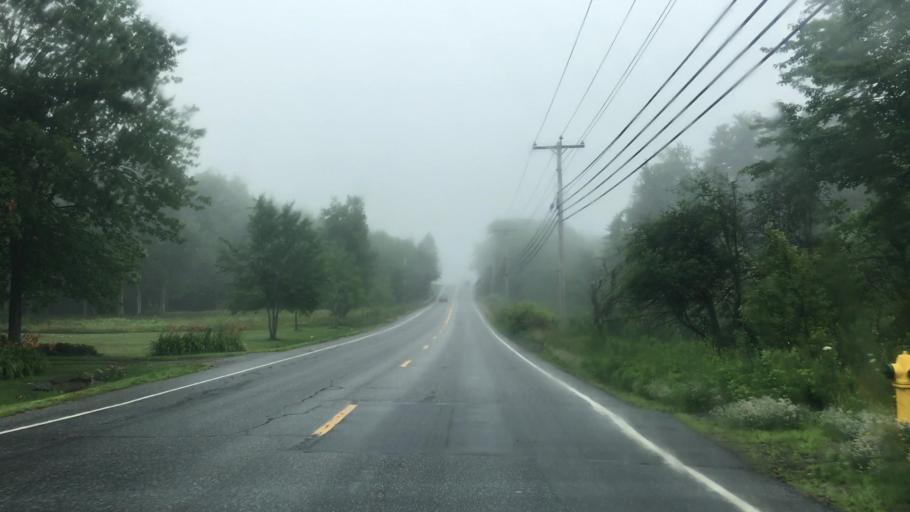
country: US
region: Maine
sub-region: Lincoln County
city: Boothbay
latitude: 43.8714
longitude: -69.6318
